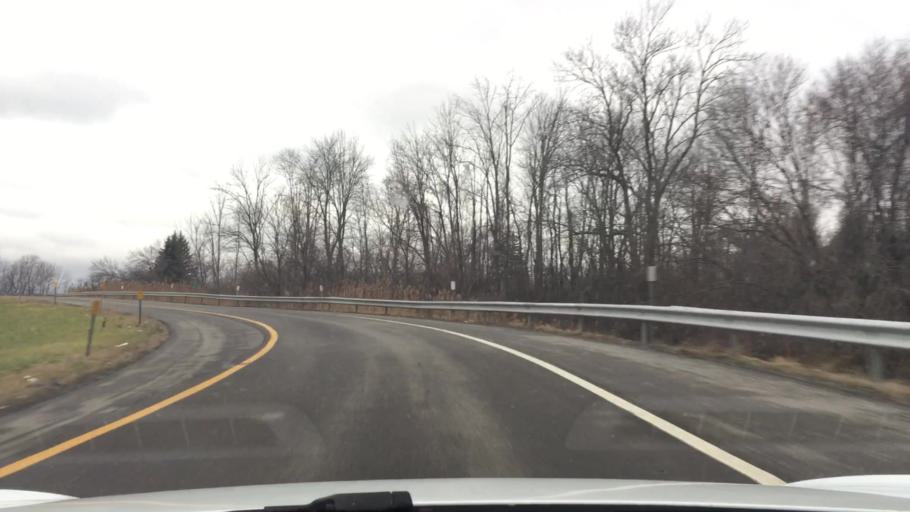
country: US
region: New York
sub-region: Erie County
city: Grandyle Village
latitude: 43.0748
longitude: -78.9416
